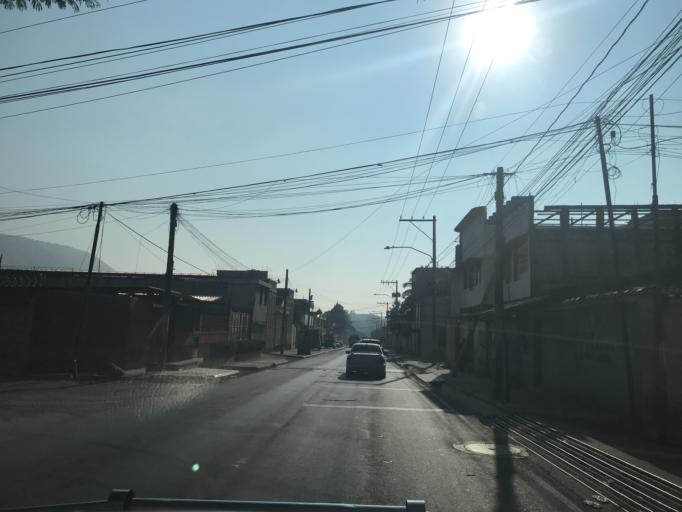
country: GT
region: Guatemala
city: Amatitlan
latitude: 14.4876
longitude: -90.6215
